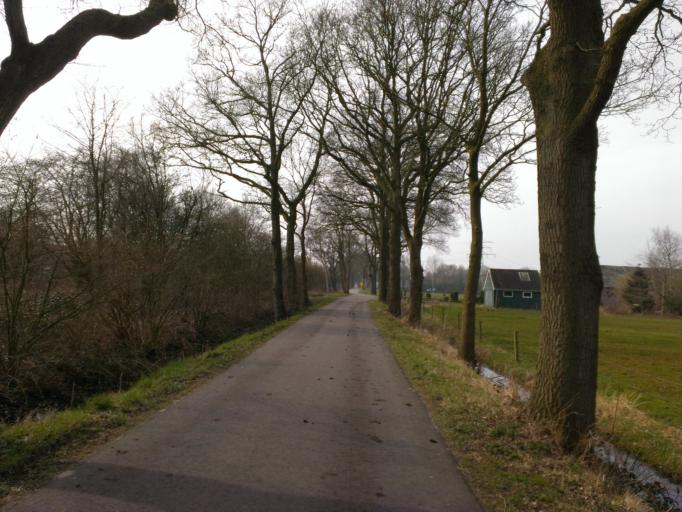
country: NL
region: Drenthe
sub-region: Gemeente Hoogeveen
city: Hoogeveen
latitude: 52.7370
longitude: 6.5072
